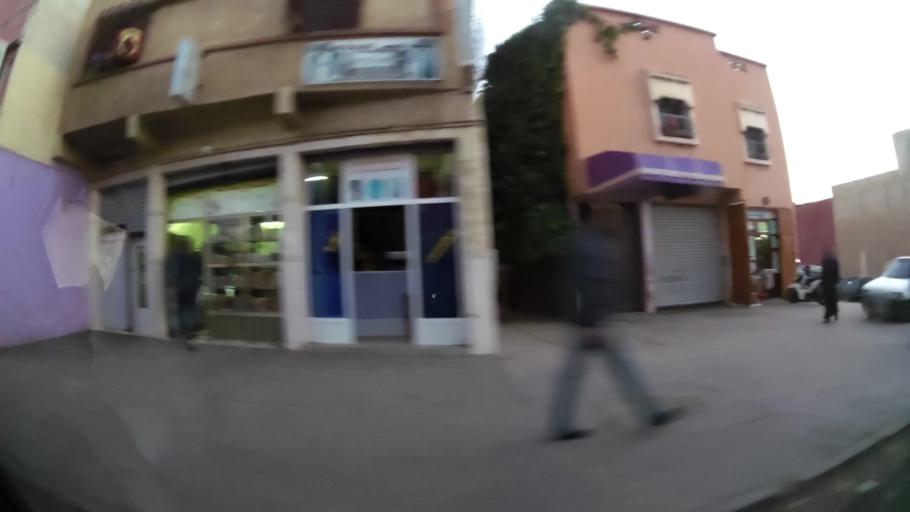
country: MA
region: Souss-Massa-Draa
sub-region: Inezgane-Ait Mellou
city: Inezgane
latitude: 30.3750
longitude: -9.4931
